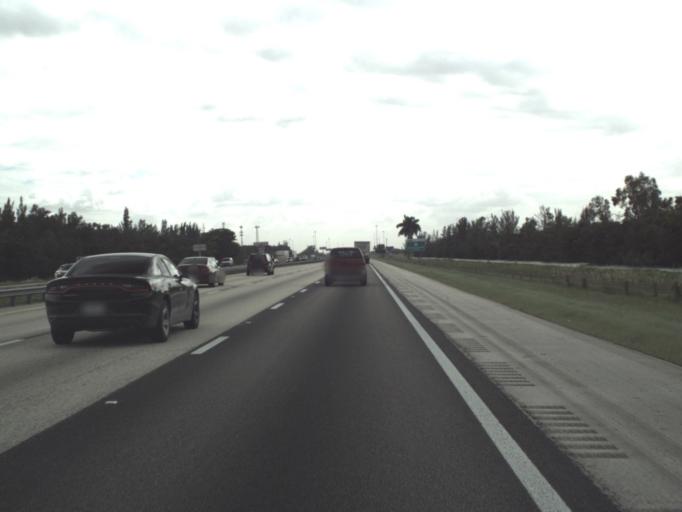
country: US
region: Florida
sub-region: Miami-Dade County
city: Palm Springs North
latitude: 25.9173
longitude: -80.3795
